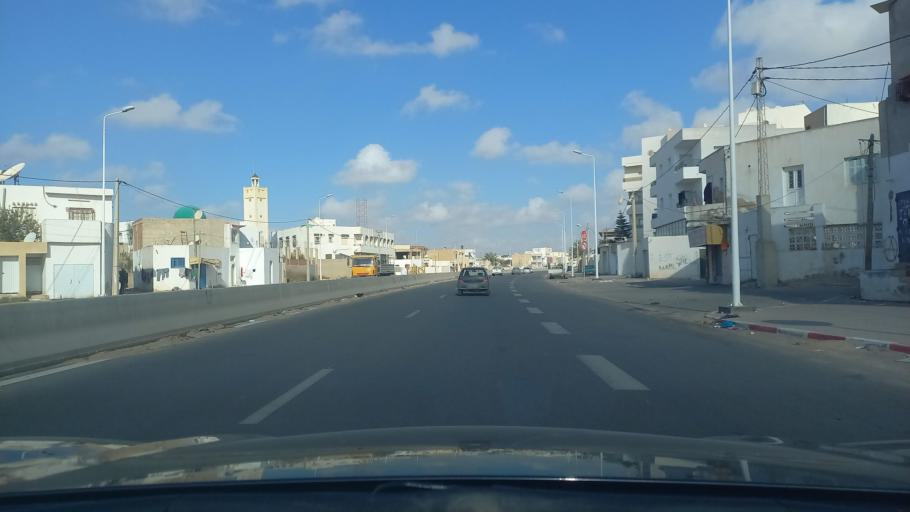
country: TN
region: Safaqis
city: Sfax
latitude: 34.7393
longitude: 10.7238
